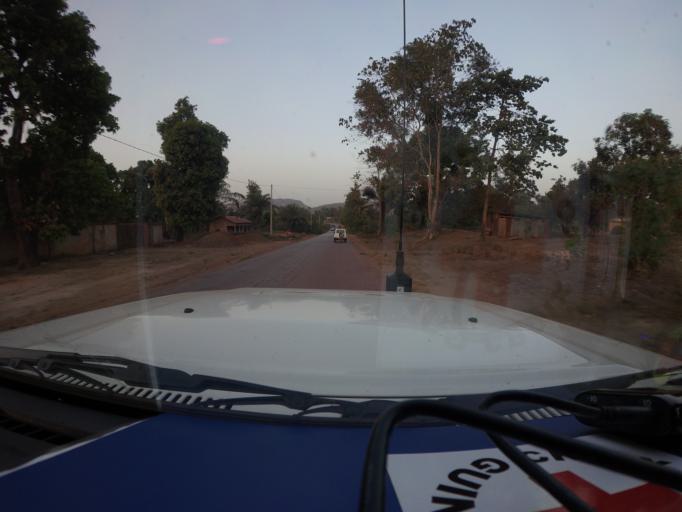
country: GN
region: Kindia
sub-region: Kindia
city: Kindia
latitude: 9.8542
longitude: -13.0860
